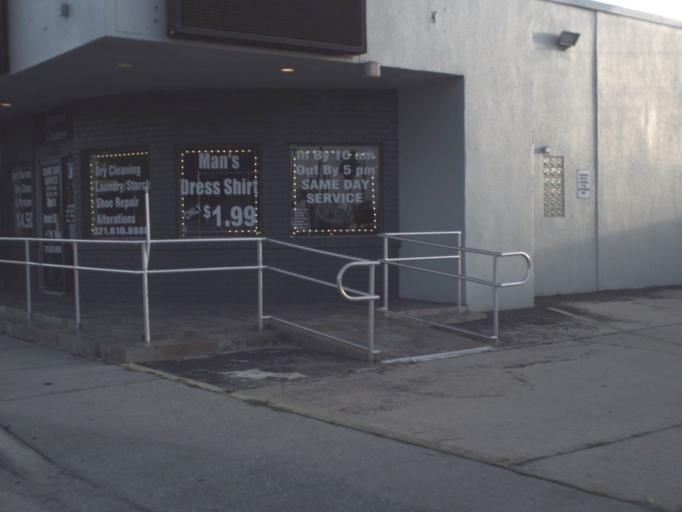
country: US
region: Florida
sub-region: Brevard County
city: Indian Harbour Beach
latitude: 28.1278
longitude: -80.6303
